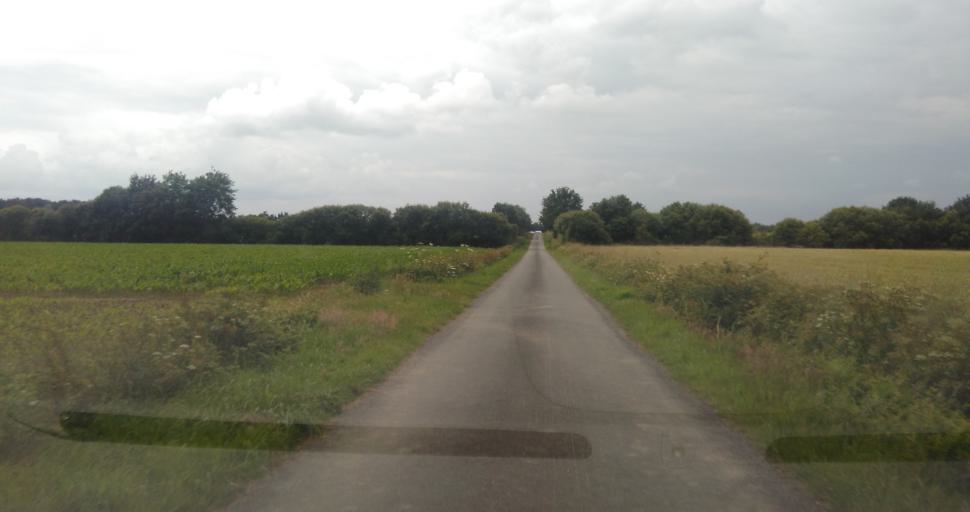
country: FR
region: Pays de la Loire
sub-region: Departement de la Vendee
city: Saint-Georges-de-Montaigu
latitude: 46.9285
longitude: -1.3201
